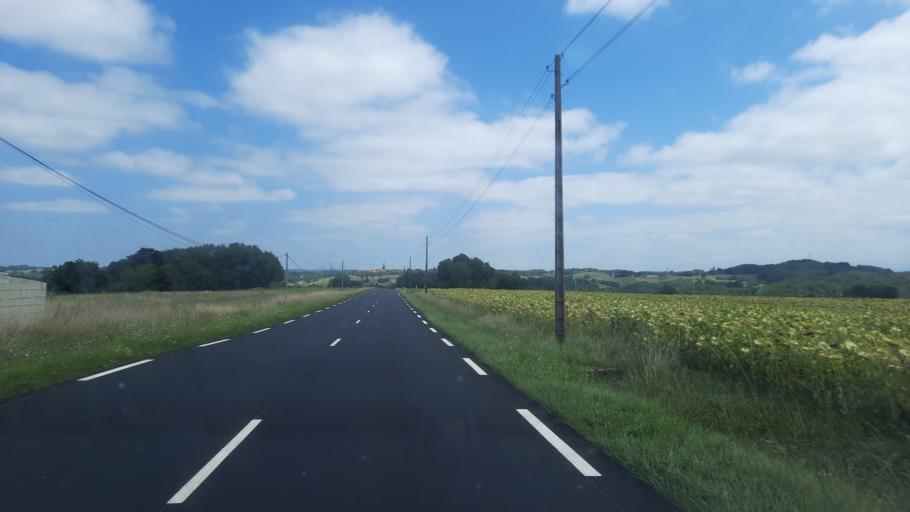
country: FR
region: Midi-Pyrenees
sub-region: Departement de la Haute-Garonne
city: Boulogne-sur-Gesse
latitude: 43.2989
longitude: 0.6085
